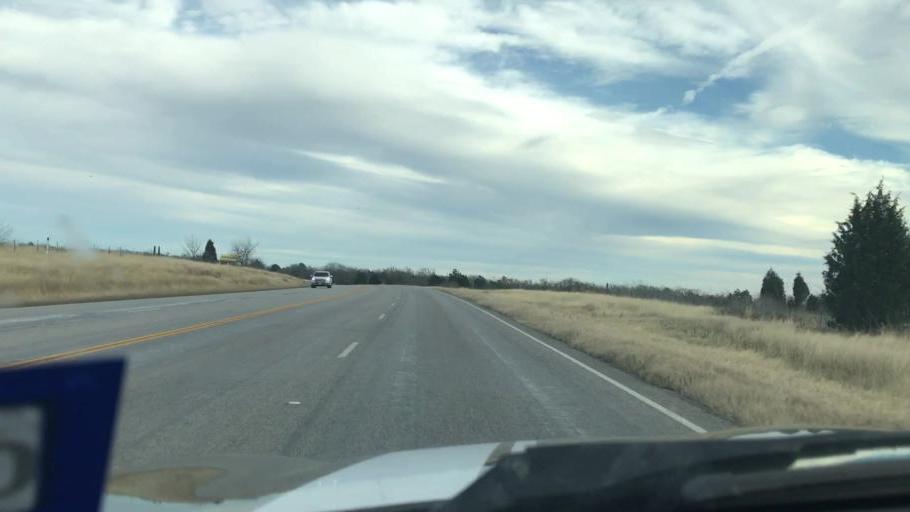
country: US
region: Texas
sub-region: Bastrop County
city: Elgin
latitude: 30.2971
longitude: -97.2824
